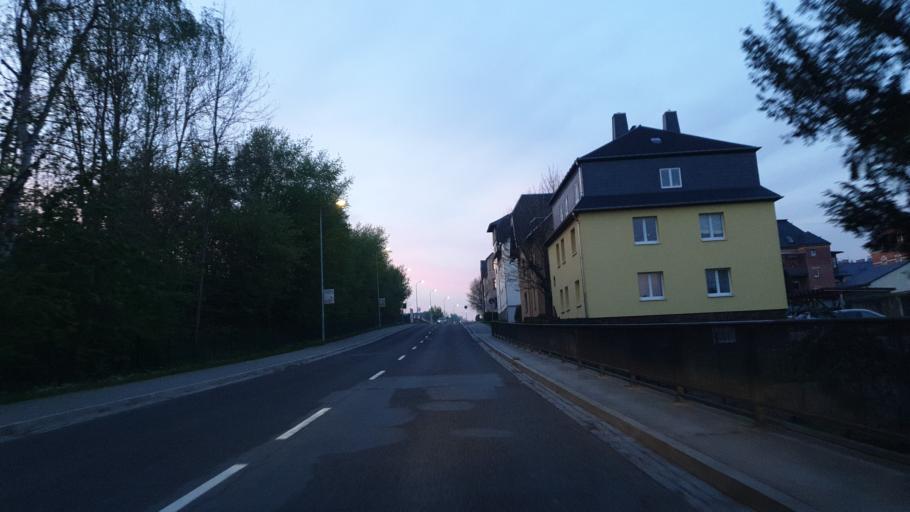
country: DE
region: Saxony
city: Stollberg
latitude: 50.7066
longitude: 12.7720
